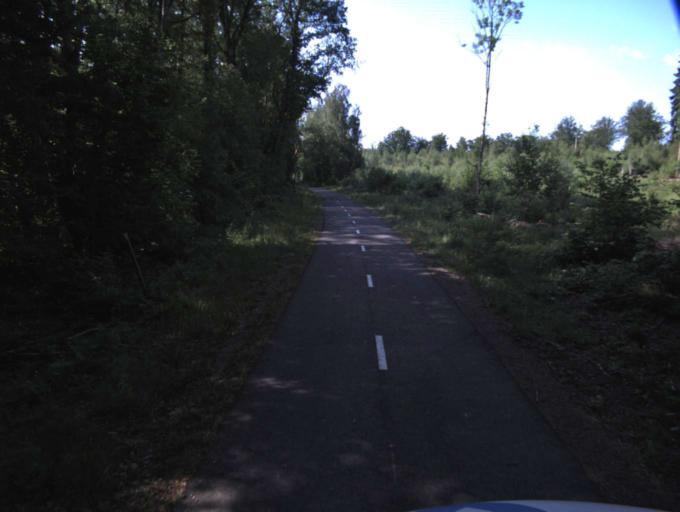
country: SE
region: Skane
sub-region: Kristianstads Kommun
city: Tollarp
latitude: 56.1468
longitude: 14.2587
